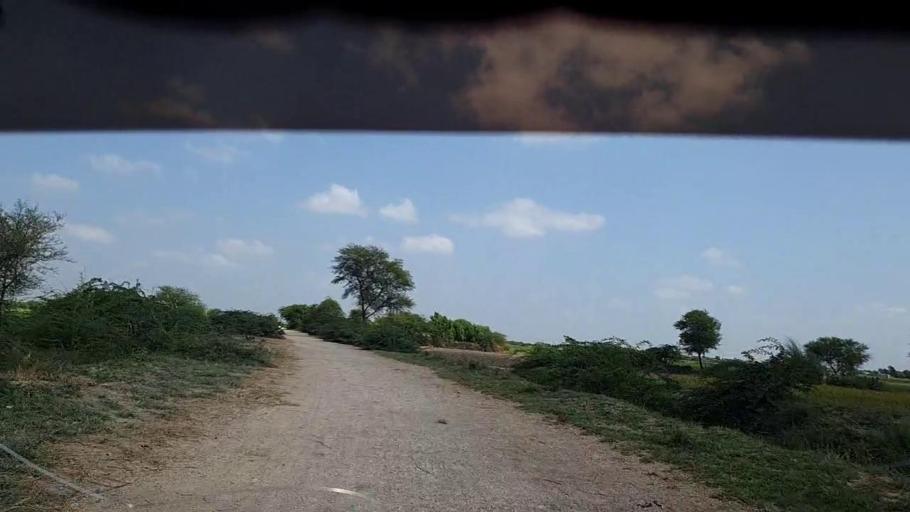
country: PK
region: Sindh
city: Kadhan
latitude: 24.6032
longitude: 68.9791
